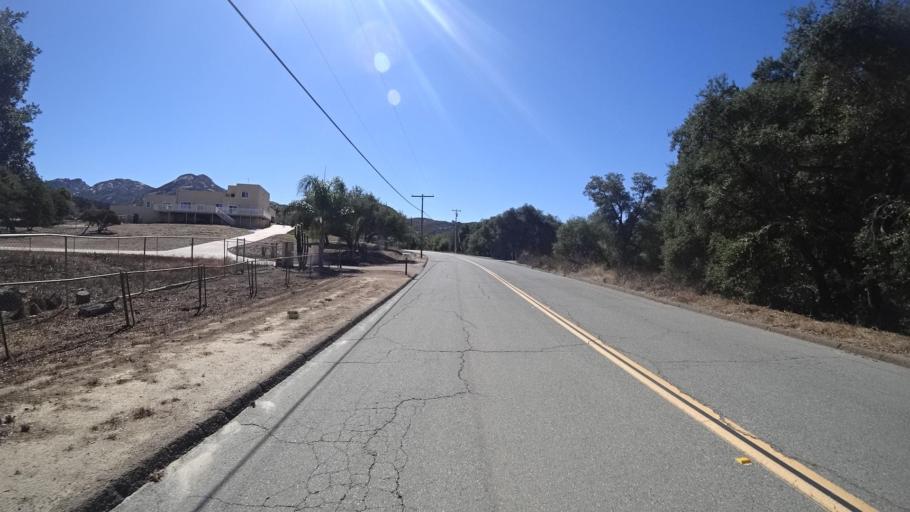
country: US
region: California
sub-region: San Diego County
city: Alpine
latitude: 32.7463
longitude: -116.7552
